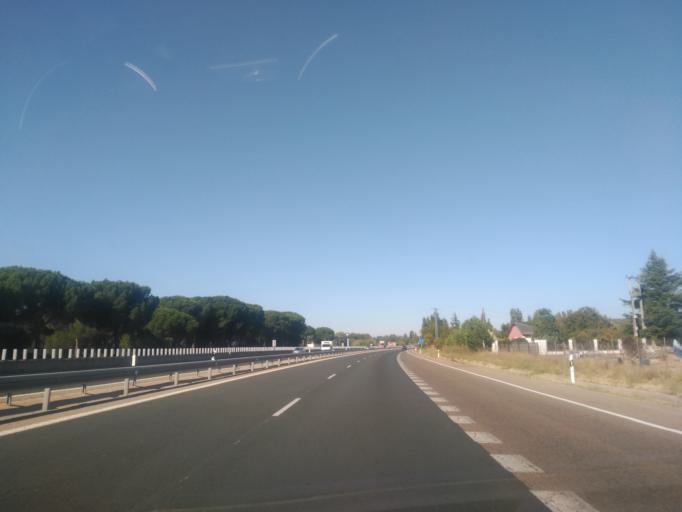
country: ES
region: Castille and Leon
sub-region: Provincia de Valladolid
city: Tudela de Duero
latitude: 41.5912
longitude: -4.6039
